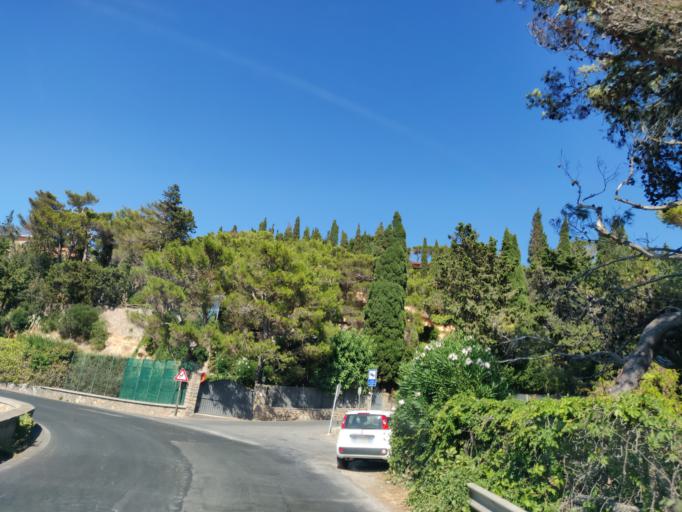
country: IT
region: Tuscany
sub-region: Provincia di Grosseto
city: Monte Argentario
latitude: 42.4342
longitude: 11.1481
